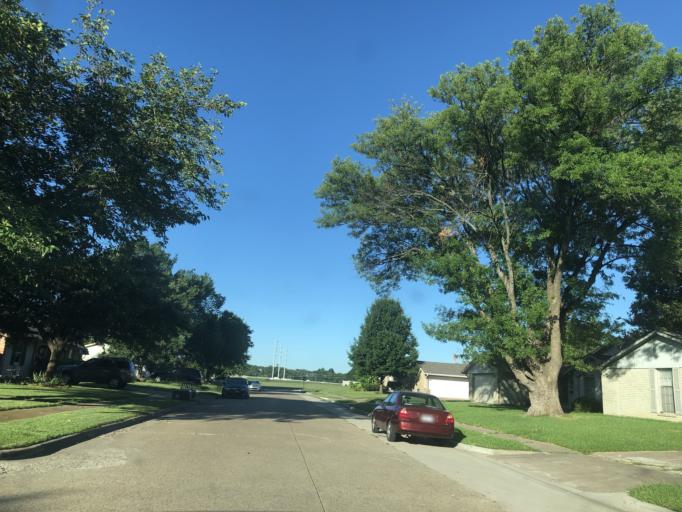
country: US
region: Texas
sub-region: Dallas County
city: Garland
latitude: 32.8472
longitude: -96.6315
